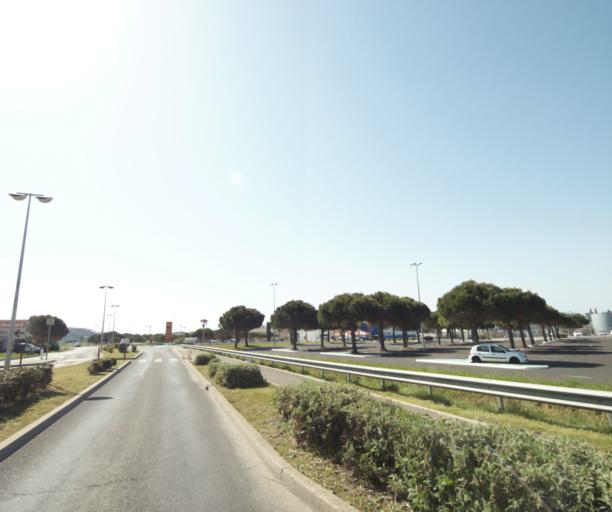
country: FR
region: Languedoc-Roussillon
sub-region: Departement de l'Herault
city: Lattes
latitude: 43.5853
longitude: 3.9300
